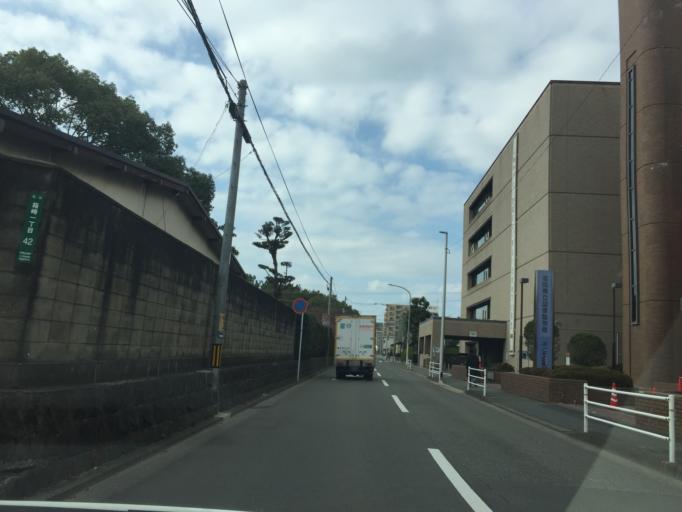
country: JP
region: Fukuoka
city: Fukuoka-shi
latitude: 33.6157
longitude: 130.4219
